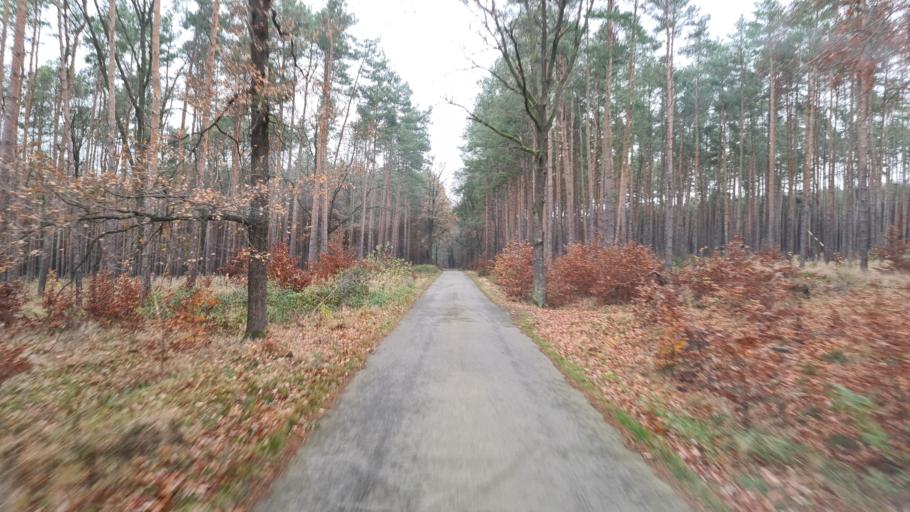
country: DE
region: Brandenburg
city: Groden
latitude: 51.3837
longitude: 13.5557
